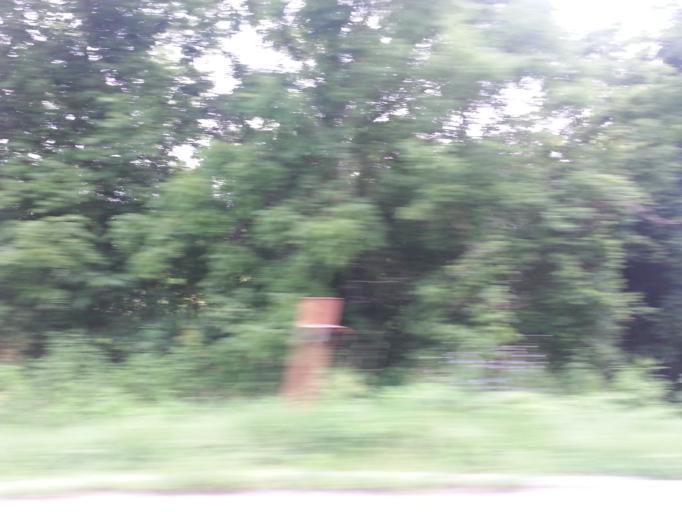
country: US
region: Kentucky
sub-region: Robertson County
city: Mount Olivet
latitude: 38.5118
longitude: -84.1479
